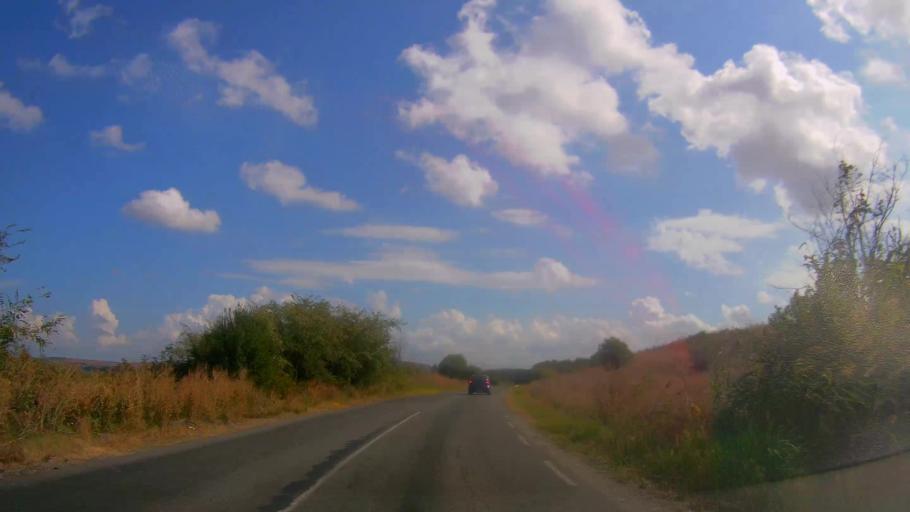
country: BG
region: Burgas
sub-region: Obshtina Kameno
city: Kameno
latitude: 42.4907
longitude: 27.3379
